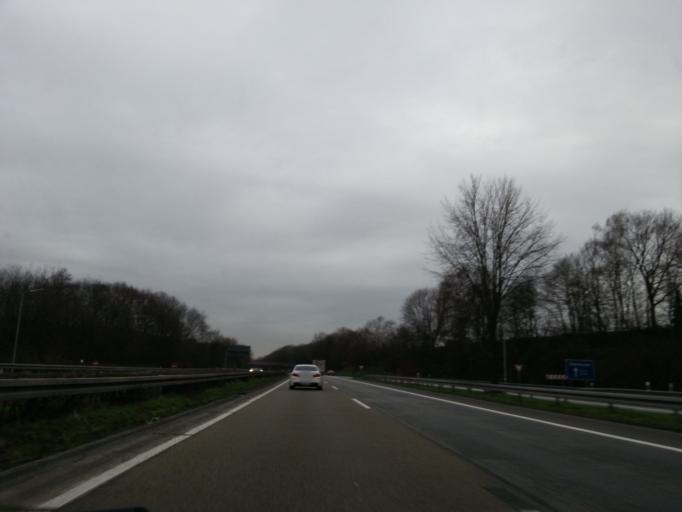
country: DE
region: North Rhine-Westphalia
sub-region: Regierungsbezirk Dusseldorf
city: Hunxe
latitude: 51.6351
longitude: 6.7466
